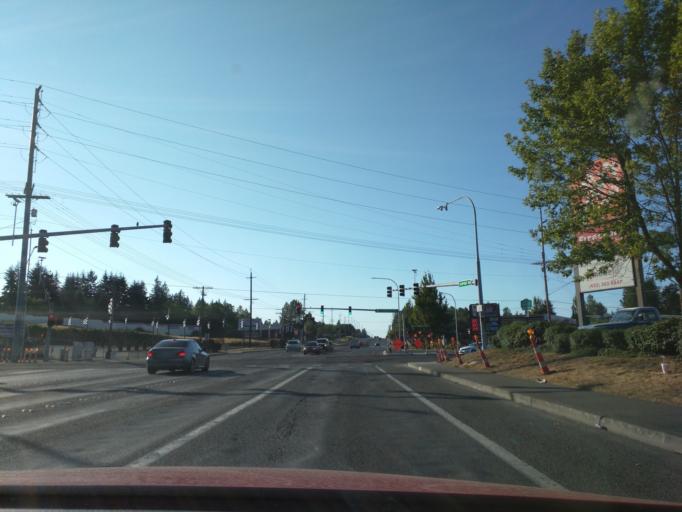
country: US
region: Washington
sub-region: Snohomish County
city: Martha Lake
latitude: 47.8890
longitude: -122.2580
